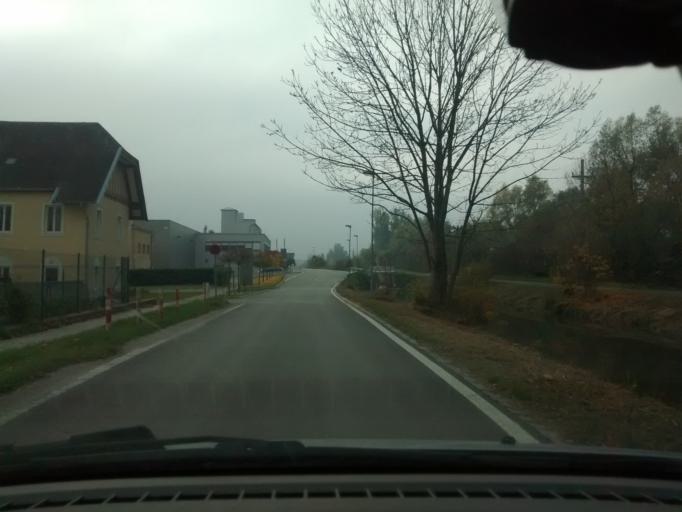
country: AT
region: Lower Austria
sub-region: Politischer Bezirk Modling
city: Guntramsdorf
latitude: 48.0422
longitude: 16.2982
